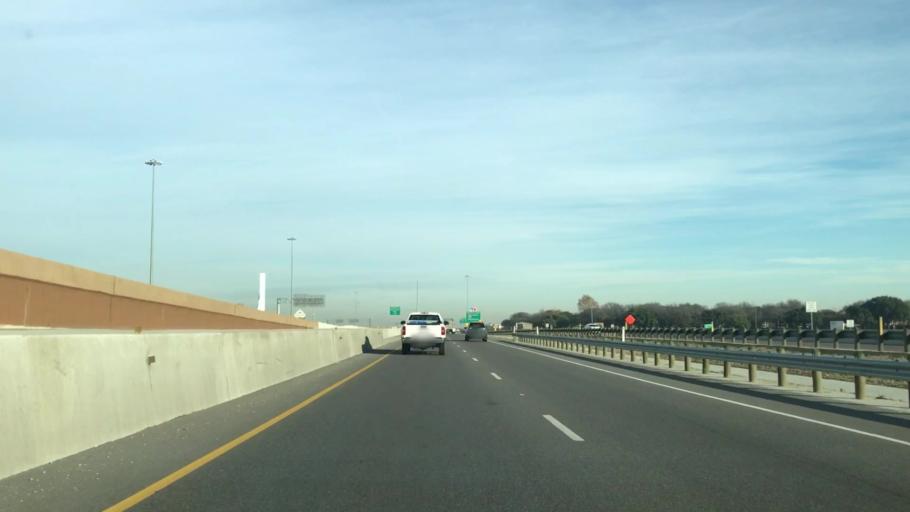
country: US
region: Texas
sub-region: Tarrant County
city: Blue Mound
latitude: 32.8450
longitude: -97.3124
